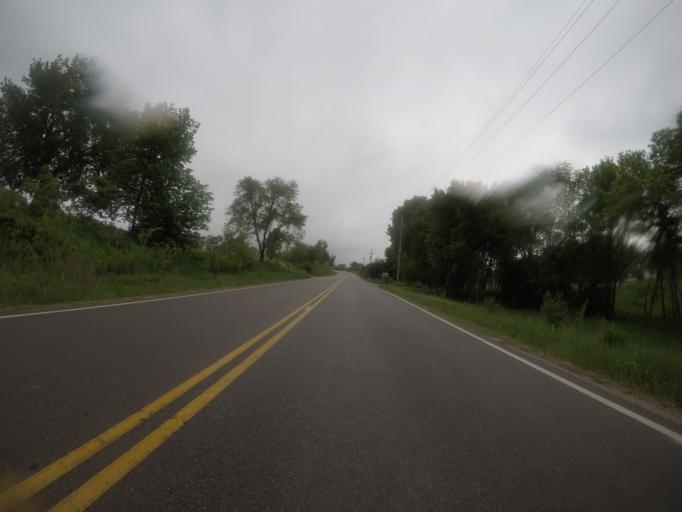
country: US
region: Kansas
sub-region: Pottawatomie County
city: Westmoreland
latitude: 39.4844
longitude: -96.1709
